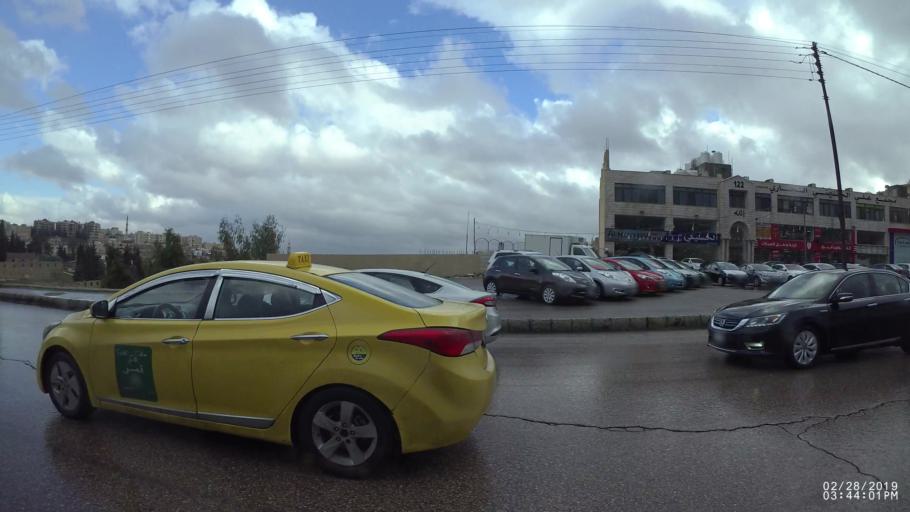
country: JO
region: Amman
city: Amman
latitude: 31.9919
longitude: 35.9145
